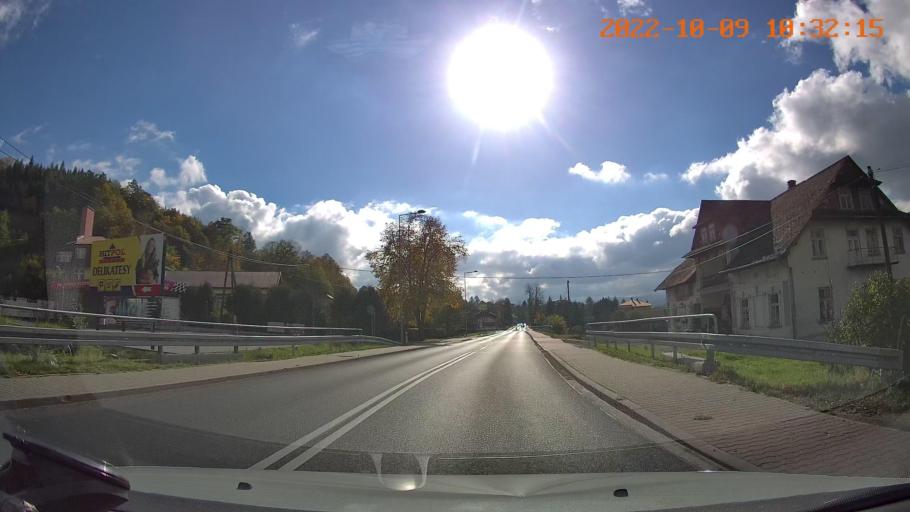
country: PL
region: Lesser Poland Voivodeship
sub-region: Powiat limanowski
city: Mszana Dolna
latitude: 49.7025
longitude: 20.0376
